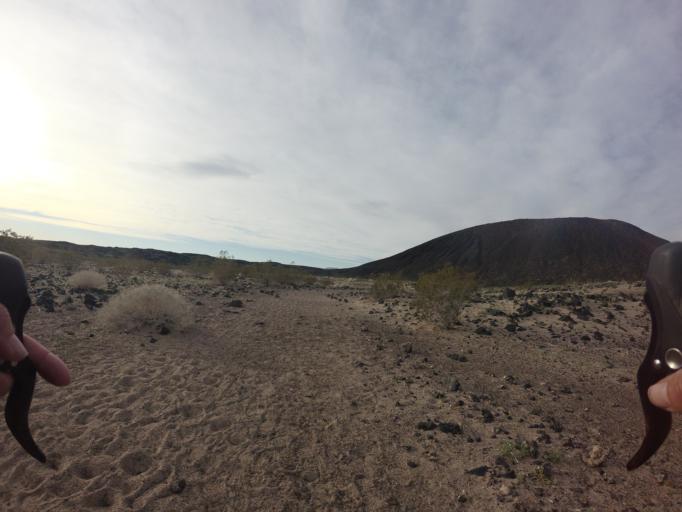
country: US
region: California
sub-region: San Bernardino County
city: Twentynine Palms
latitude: 34.5480
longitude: -115.7875
